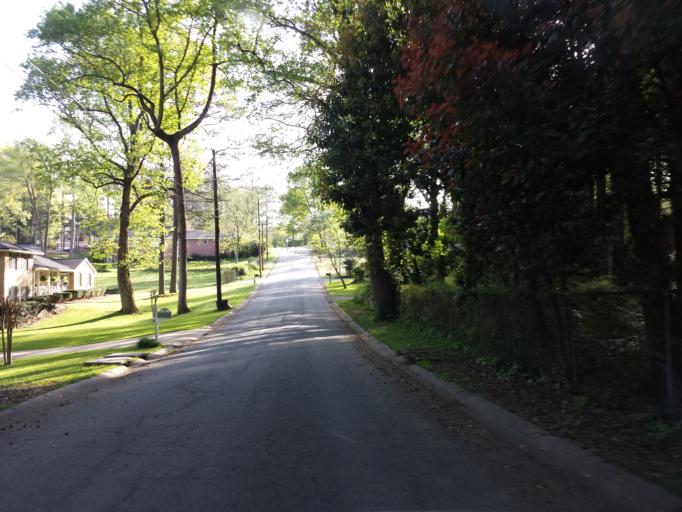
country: US
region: Georgia
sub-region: Cobb County
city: Marietta
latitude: 33.9688
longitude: -84.5405
